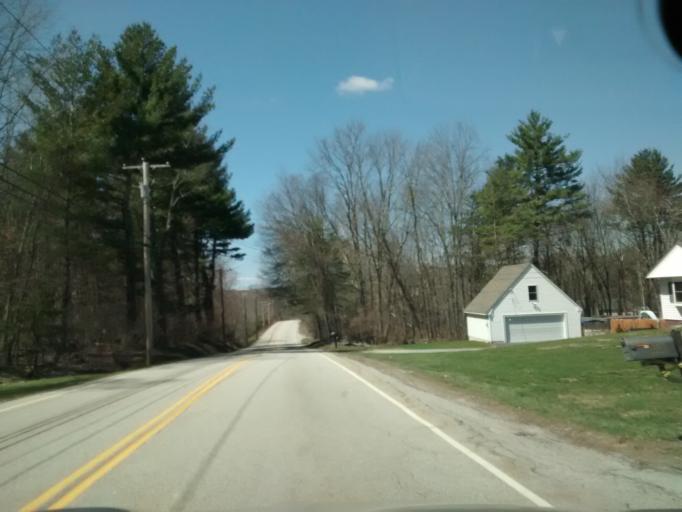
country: US
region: Massachusetts
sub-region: Worcester County
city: Oxford
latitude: 42.1123
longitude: -71.8381
